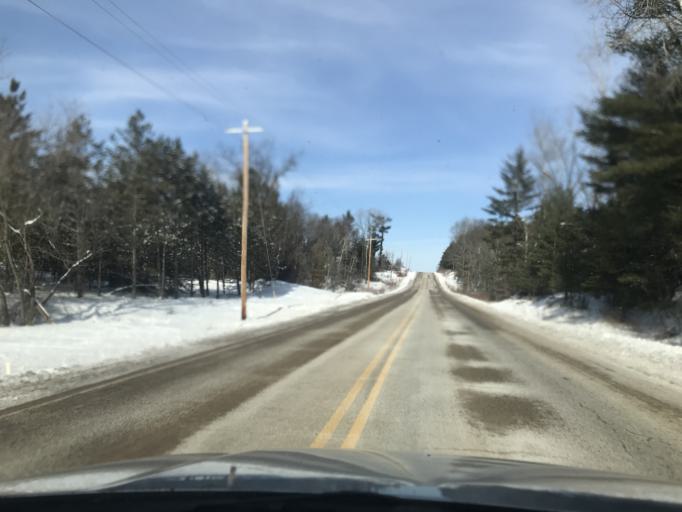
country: US
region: Wisconsin
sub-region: Oconto County
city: Oconto Falls
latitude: 45.1404
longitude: -88.1772
